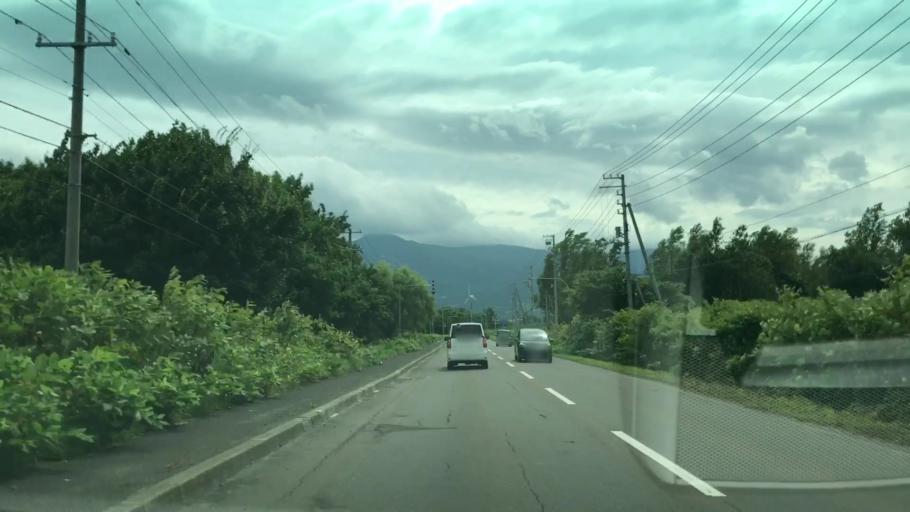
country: JP
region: Hokkaido
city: Iwanai
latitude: 43.0045
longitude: 140.5422
